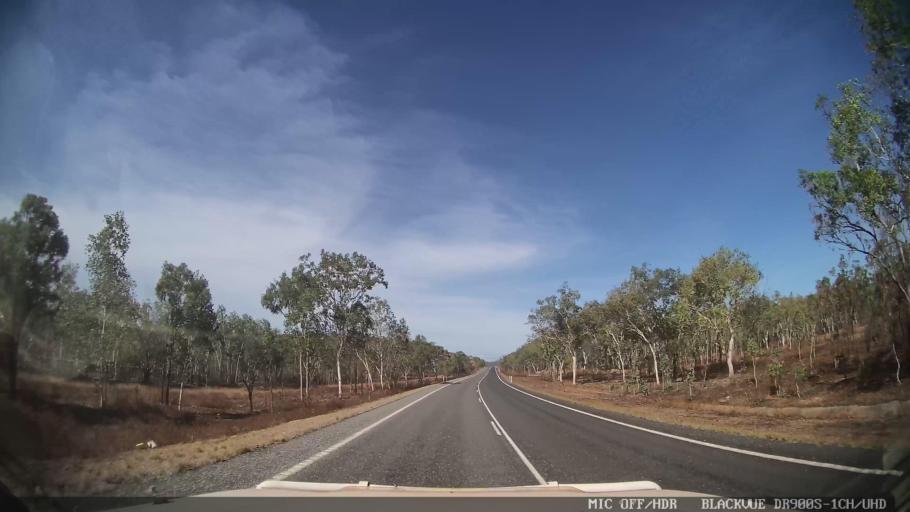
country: AU
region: Queensland
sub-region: Cook
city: Cooktown
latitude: -15.6968
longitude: 145.0319
